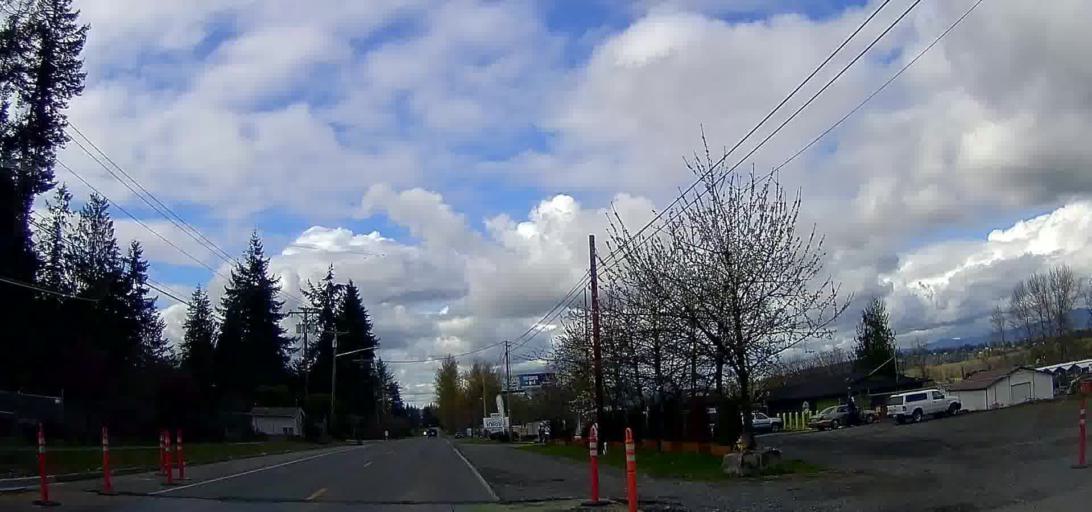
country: US
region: Washington
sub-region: Snohomish County
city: Smokey Point
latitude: 48.1698
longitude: -122.1878
